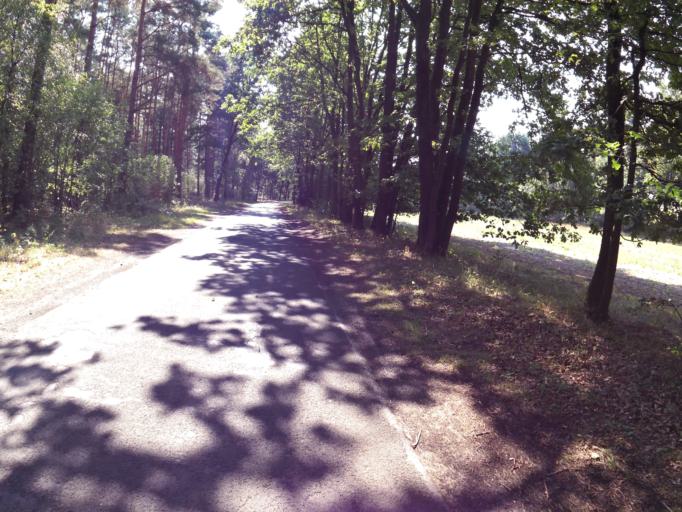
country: DE
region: North Rhine-Westphalia
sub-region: Regierungsbezirk Detmold
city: Harsewinkel
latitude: 51.9498
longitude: 8.2354
